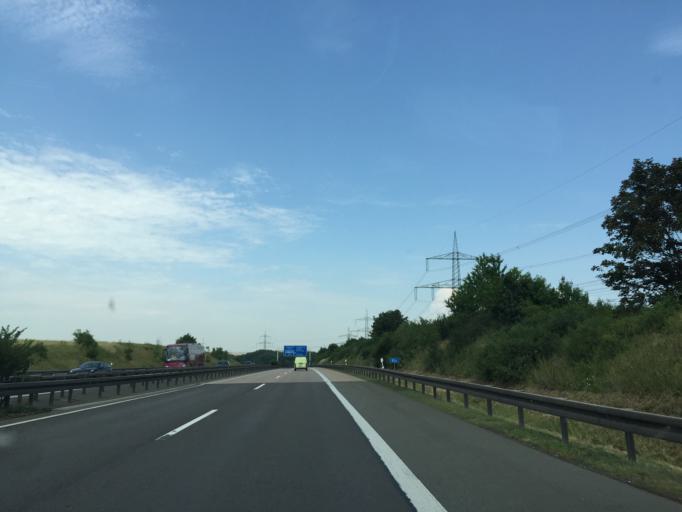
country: DE
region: Thuringia
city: Ichtershausen
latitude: 50.8849
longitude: 10.9821
